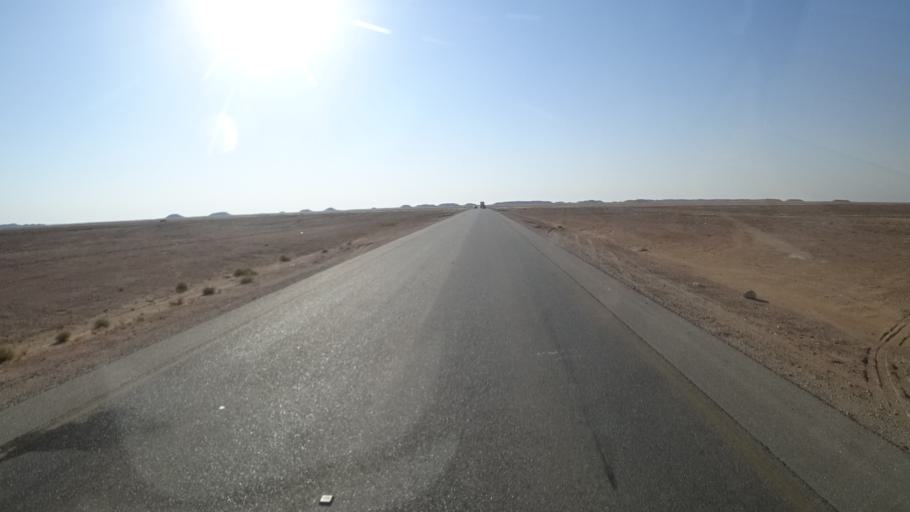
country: OM
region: Zufar
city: Salalah
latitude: 17.6423
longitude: 53.8361
